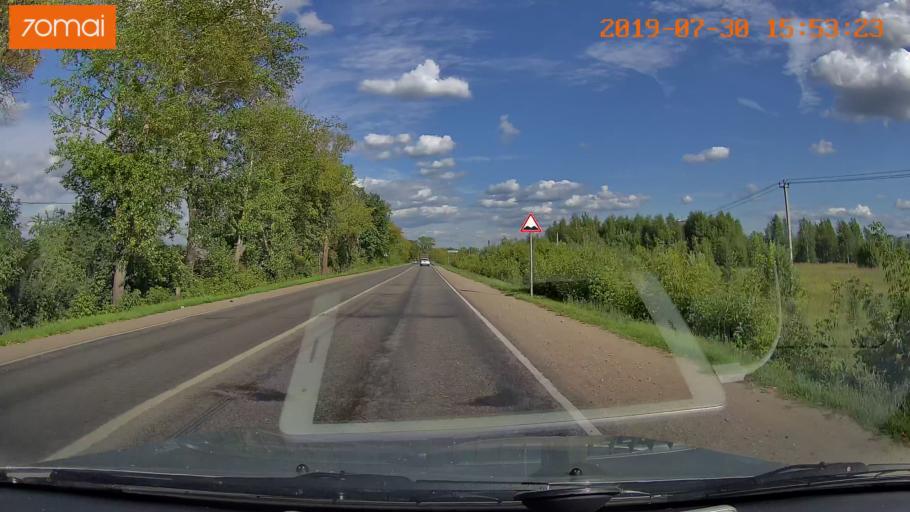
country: RU
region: Moskovskaya
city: Voskresensk
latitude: 55.3202
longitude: 38.6389
